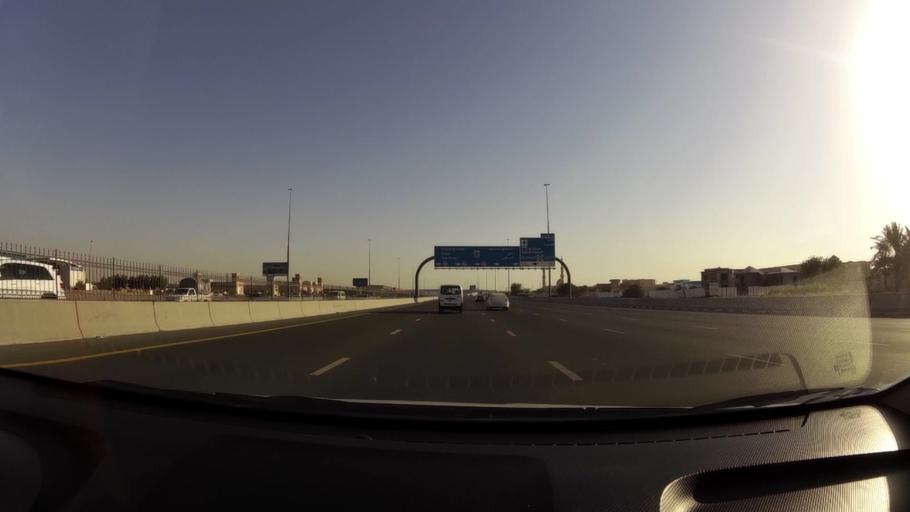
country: AE
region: Ash Shariqah
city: Sharjah
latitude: 25.3467
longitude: 55.4740
